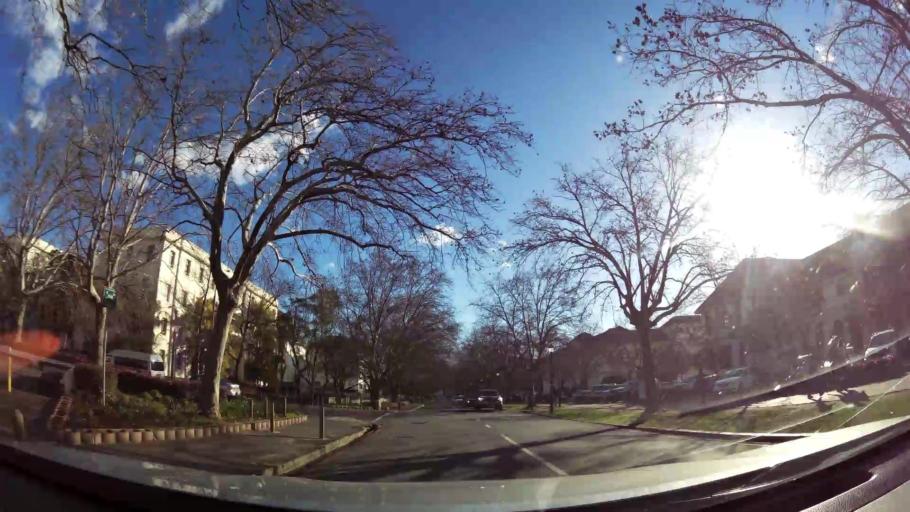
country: ZA
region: Western Cape
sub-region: Cape Winelands District Municipality
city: Stellenbosch
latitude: -33.9339
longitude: 18.8659
